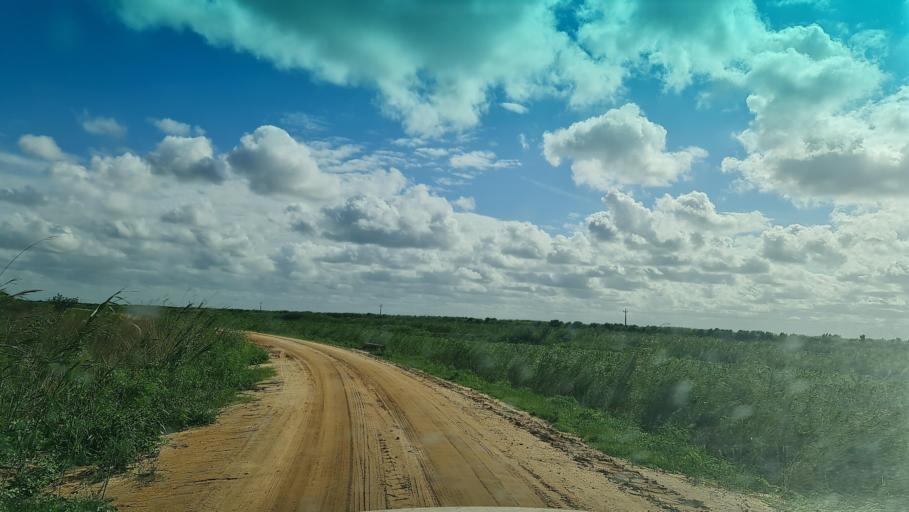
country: MZ
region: Maputo
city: Manhica
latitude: -25.4339
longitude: 32.8627
